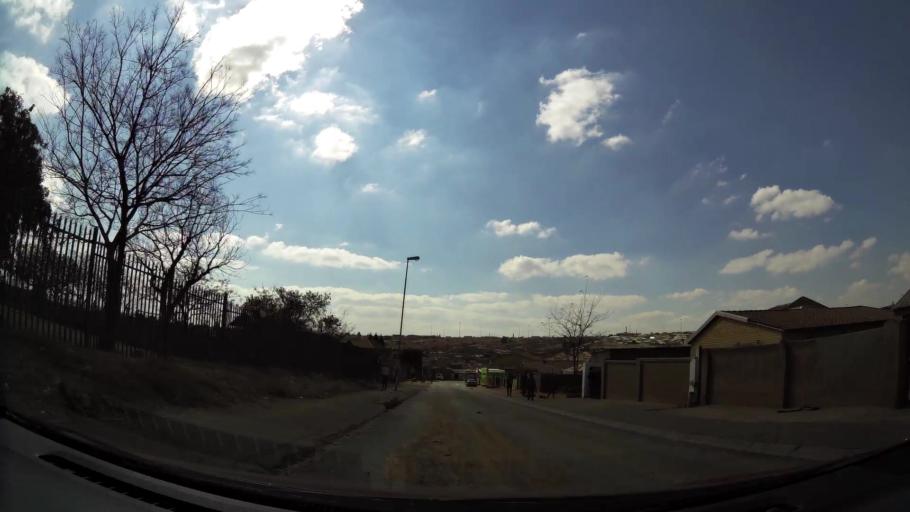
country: ZA
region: Gauteng
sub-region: Ekurhuleni Metropolitan Municipality
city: Tembisa
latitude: -26.0132
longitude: 28.1989
